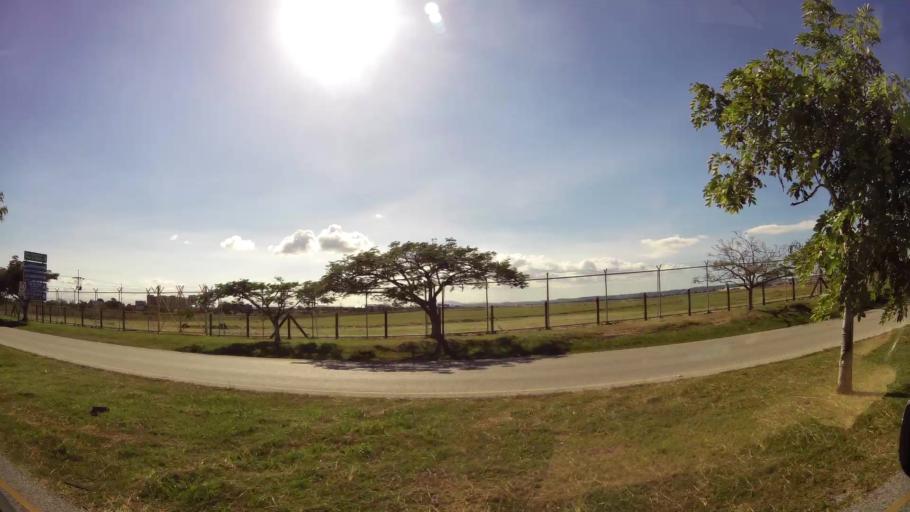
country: CR
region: Guanacaste
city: Liberia
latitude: 10.5973
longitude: -85.5284
